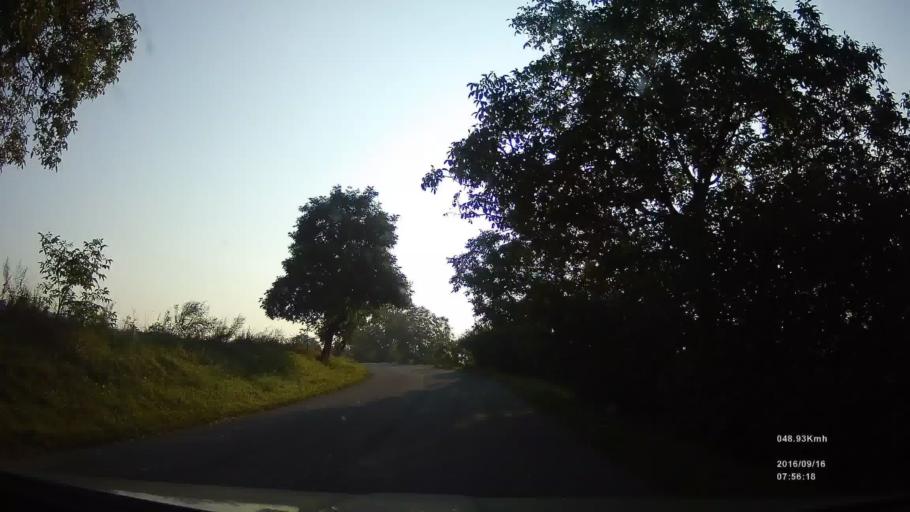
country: SK
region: Presovsky
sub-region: Okres Presov
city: Presov
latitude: 48.9139
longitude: 21.1337
